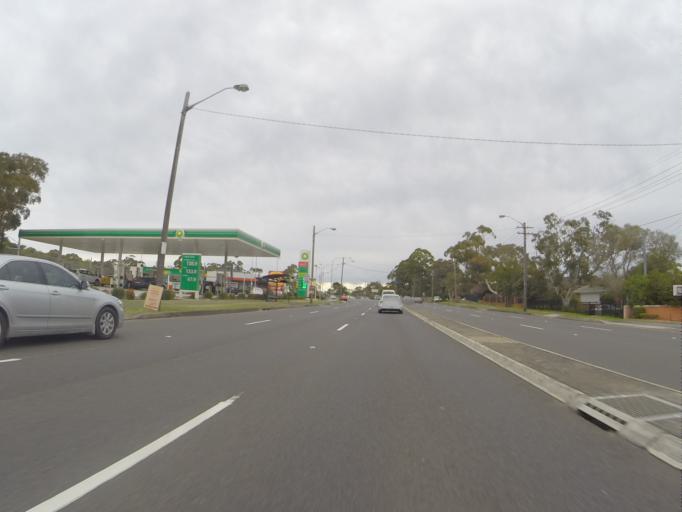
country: AU
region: New South Wales
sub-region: Sutherland Shire
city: Heathcote
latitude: -34.0770
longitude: 151.0111
